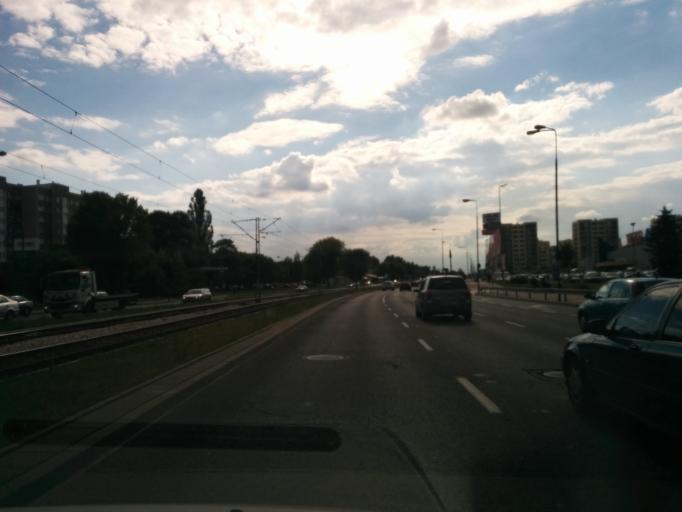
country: PL
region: Masovian Voivodeship
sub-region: Warszawa
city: Bemowo
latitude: 52.2390
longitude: 20.9093
